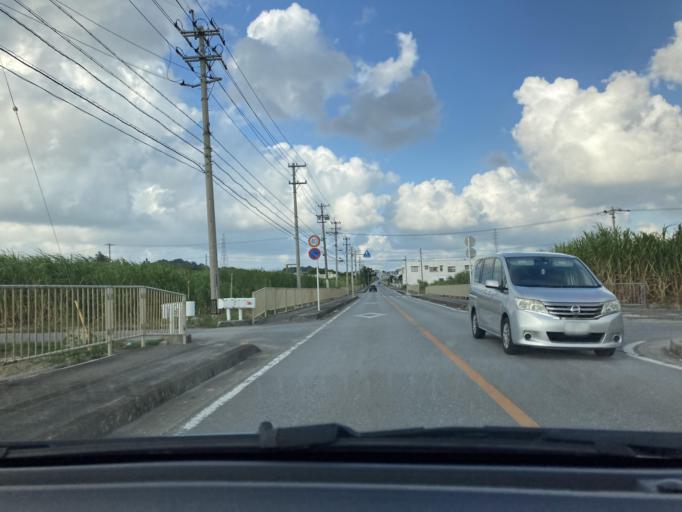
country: JP
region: Okinawa
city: Itoman
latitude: 26.1431
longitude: 127.7025
